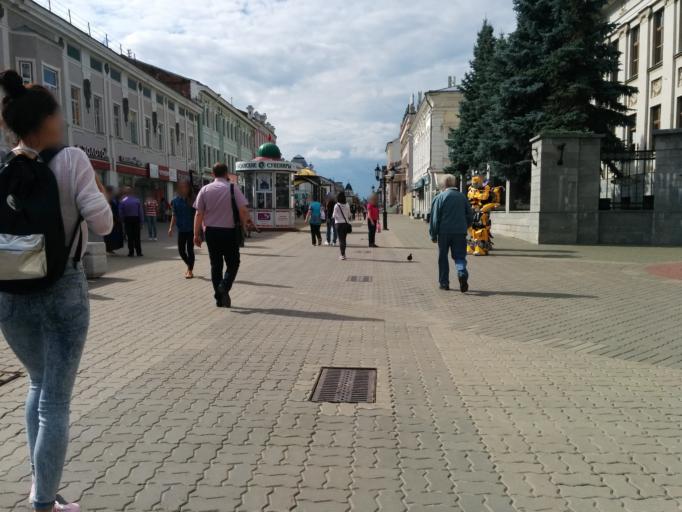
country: RU
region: Tatarstan
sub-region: Gorod Kazan'
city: Kazan
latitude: 55.7890
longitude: 49.1184
